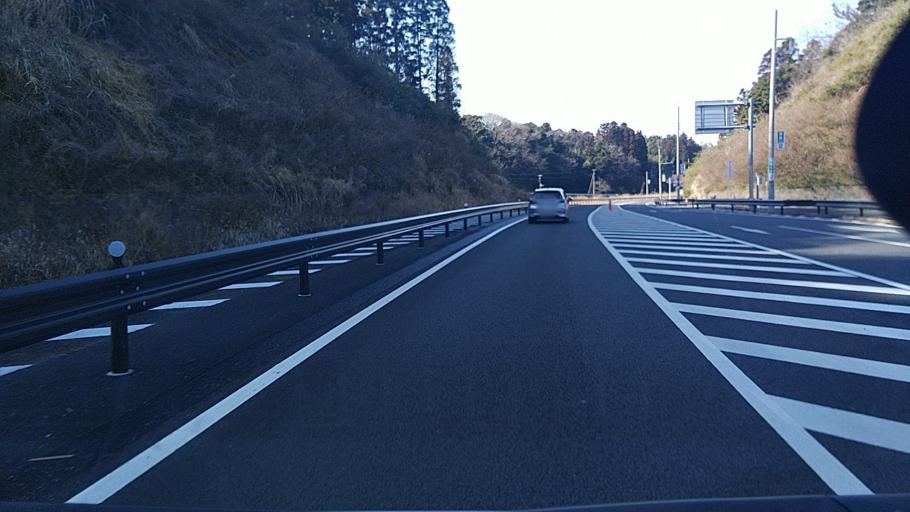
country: JP
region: Chiba
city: Mobara
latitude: 35.4015
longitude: 140.2442
